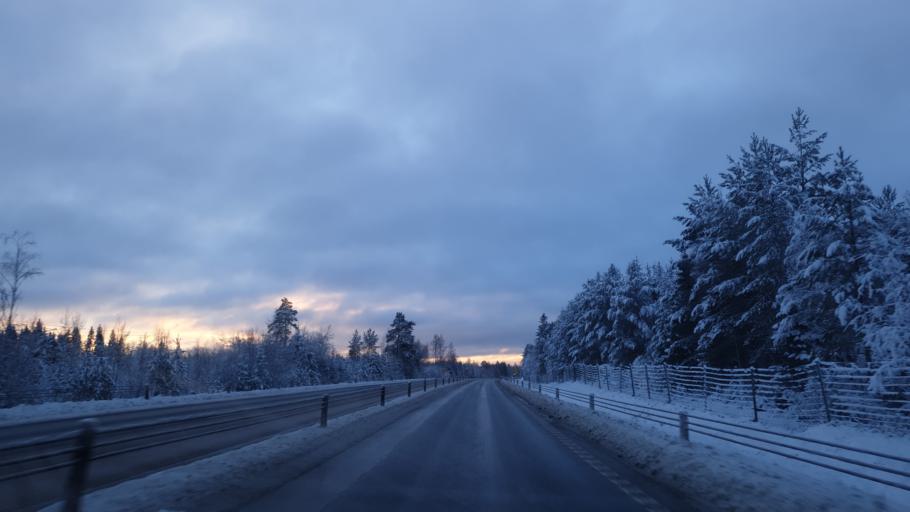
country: SE
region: Vaesterbotten
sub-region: Nordmalings Kommun
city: Nordmaling
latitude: 63.5281
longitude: 19.3911
